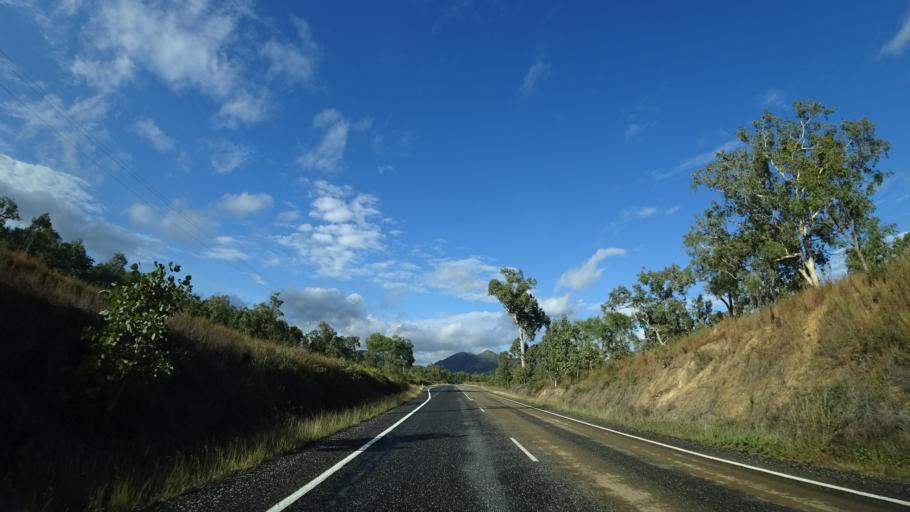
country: AU
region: Queensland
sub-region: Cook
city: Cooktown
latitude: -15.6118
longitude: 145.2213
